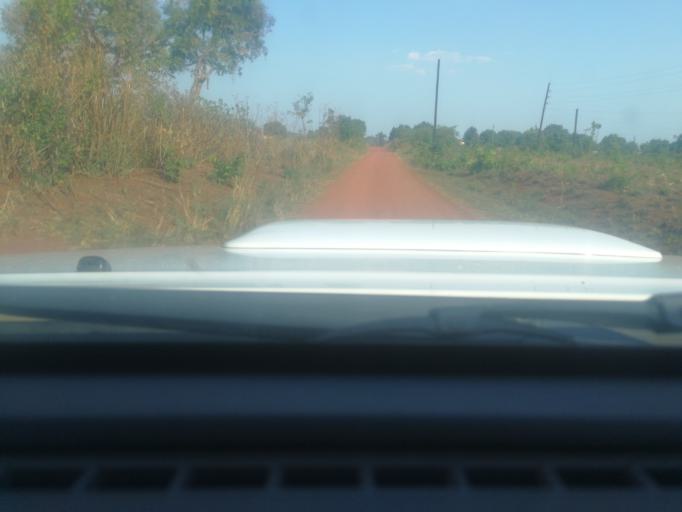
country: ZM
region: Northern
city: Kasama
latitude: -10.2150
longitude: 31.1395
